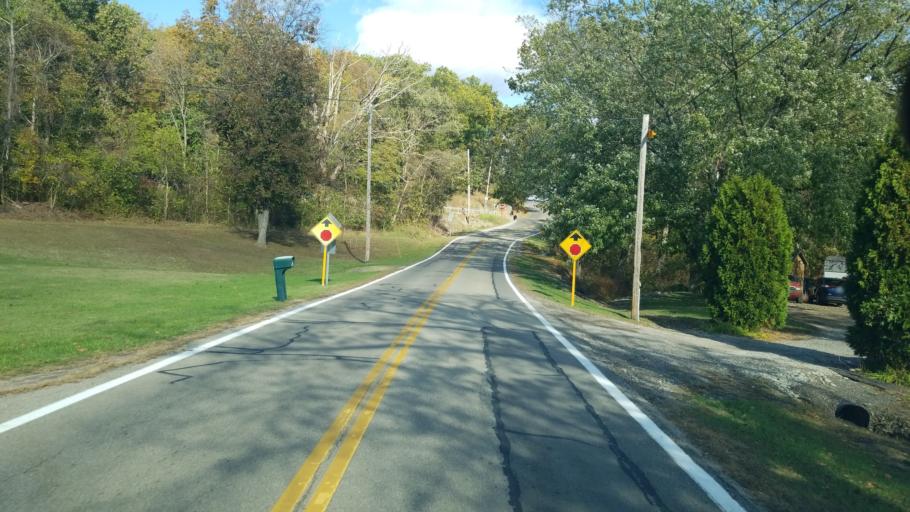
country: US
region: Ohio
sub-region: Jackson County
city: Wellston
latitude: 39.1158
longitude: -82.5613
